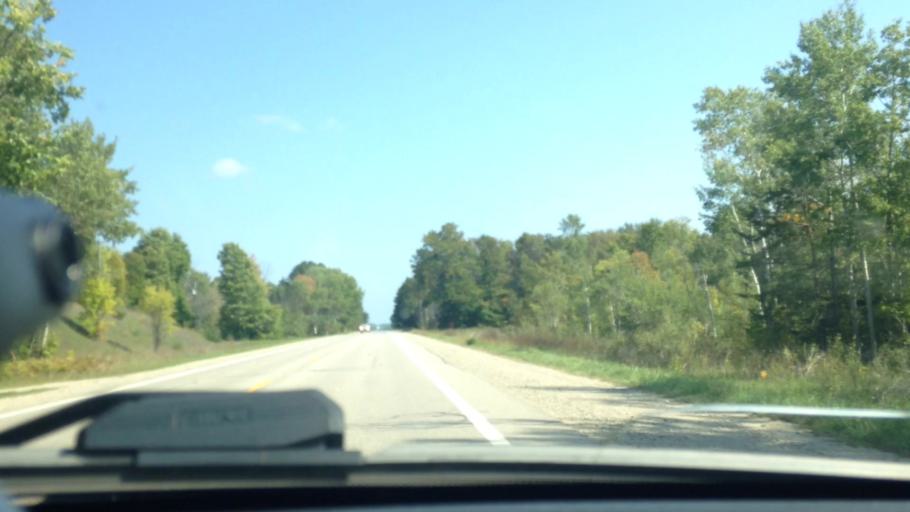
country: US
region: Michigan
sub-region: Luce County
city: Newberry
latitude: 46.3102
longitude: -85.6424
